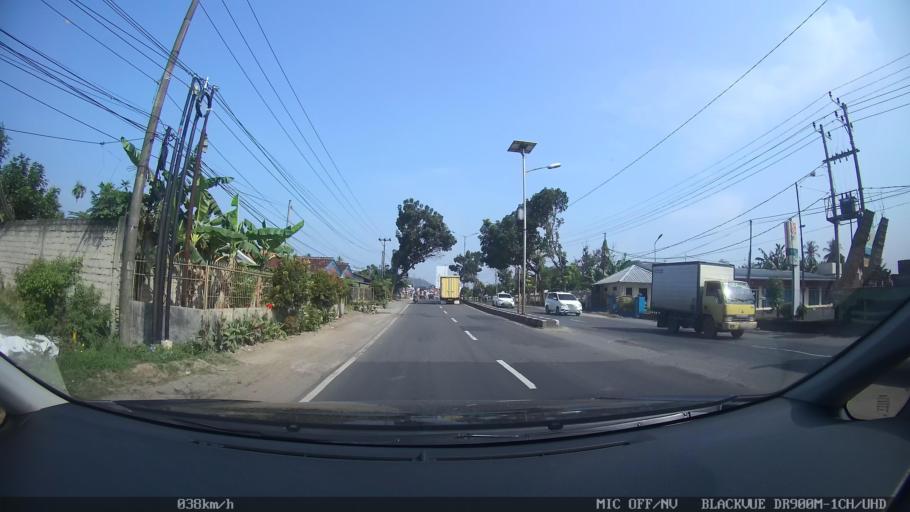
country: ID
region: Lampung
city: Natar
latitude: -5.2488
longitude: 105.1803
